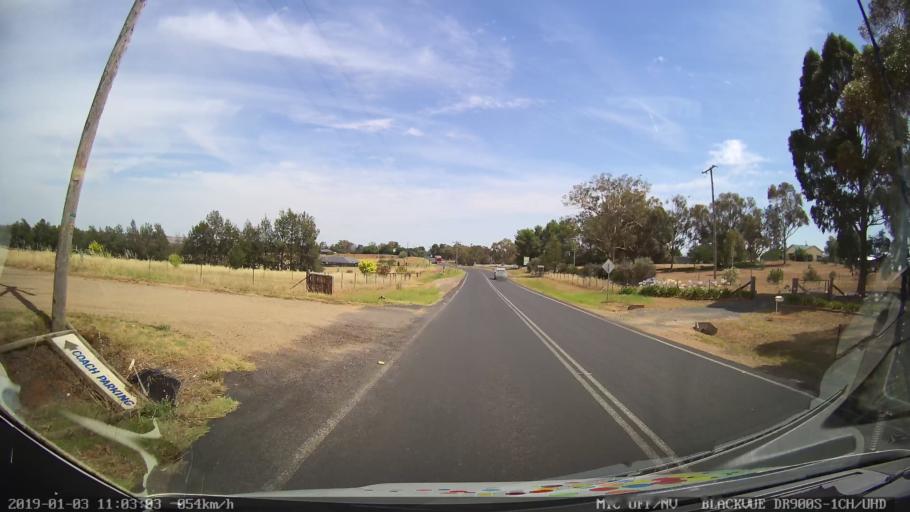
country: AU
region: New South Wales
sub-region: Young
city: Young
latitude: -34.2938
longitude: 148.2967
